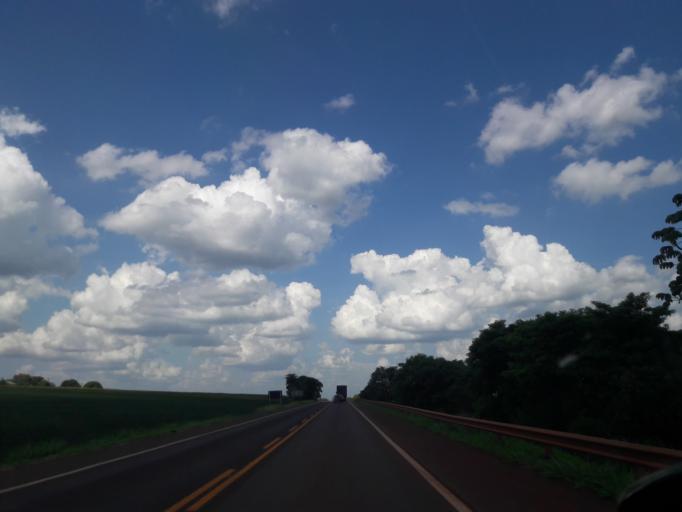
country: BR
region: Parana
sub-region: Corbelia
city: Corbelia
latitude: -24.6440
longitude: -53.2149
